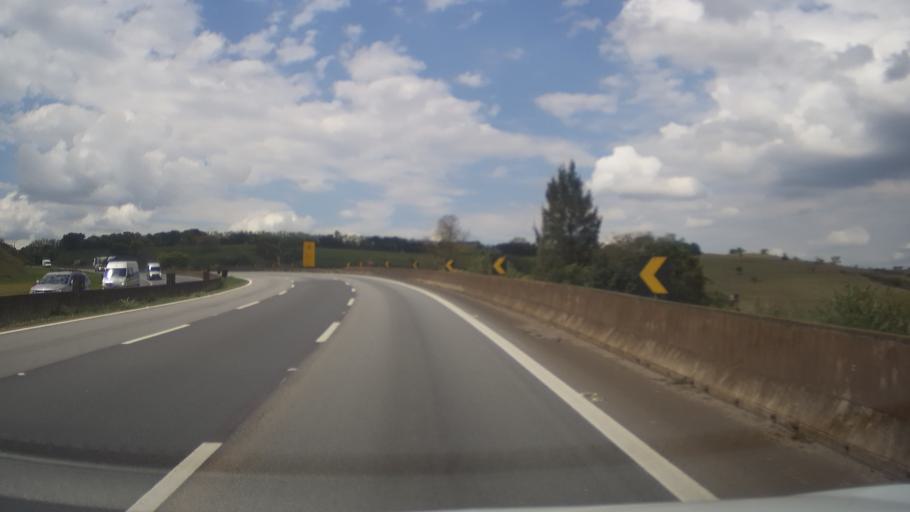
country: BR
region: Minas Gerais
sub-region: Nepomuceno
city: Nepomuceno
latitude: -21.2856
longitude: -45.1408
